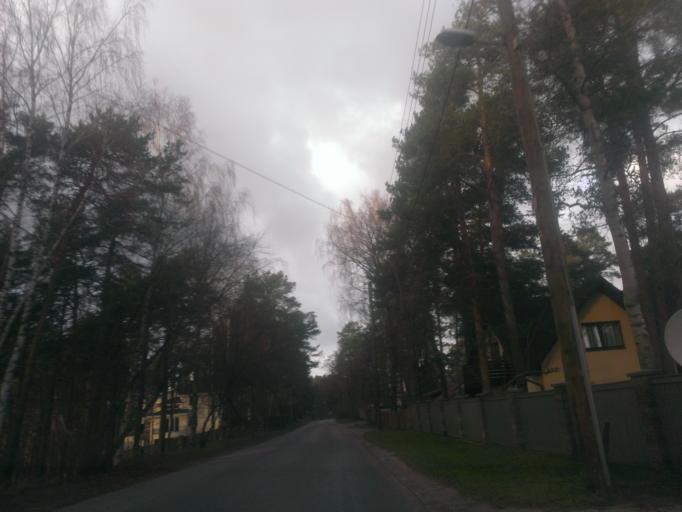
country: LV
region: Riga
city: Bergi
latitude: 56.9861
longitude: 24.2965
